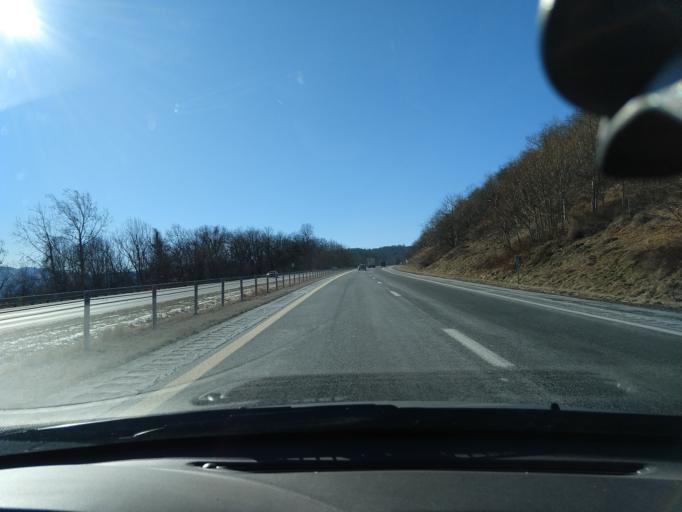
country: US
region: Virginia
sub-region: City of Waynesboro
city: Waynesboro
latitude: 38.0359
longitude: -78.8446
